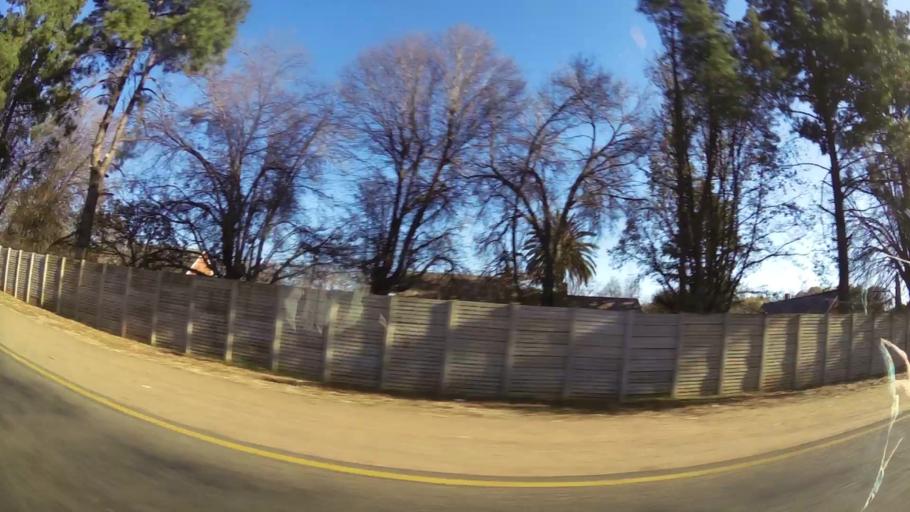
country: ZA
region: Gauteng
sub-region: Ekurhuleni Metropolitan Municipality
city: Tembisa
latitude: -26.0402
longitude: 28.2489
